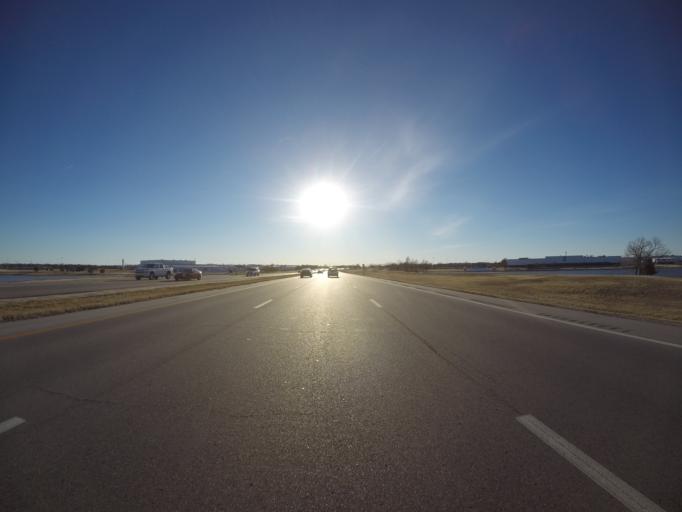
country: US
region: Kansas
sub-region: Sedgwick County
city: Wichita
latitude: 37.6416
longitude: -97.4087
